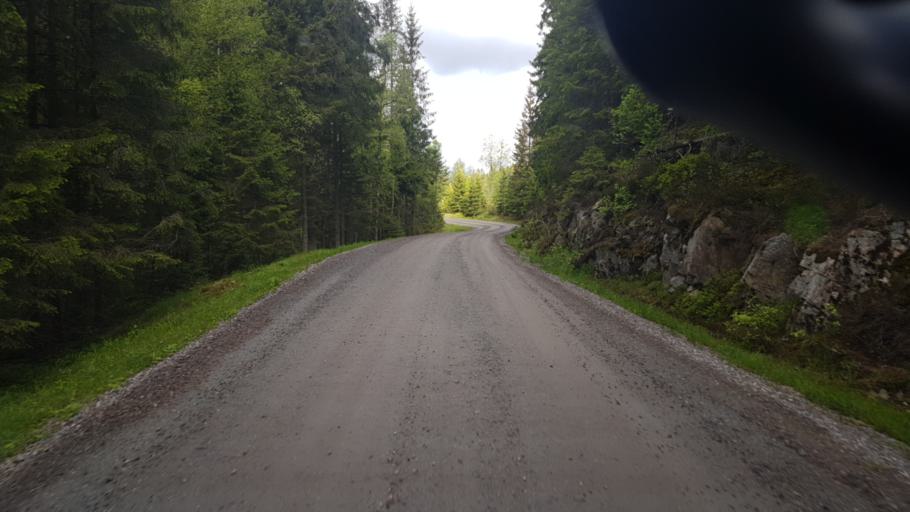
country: NO
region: Ostfold
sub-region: Romskog
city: Romskog
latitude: 59.7138
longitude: 12.0204
